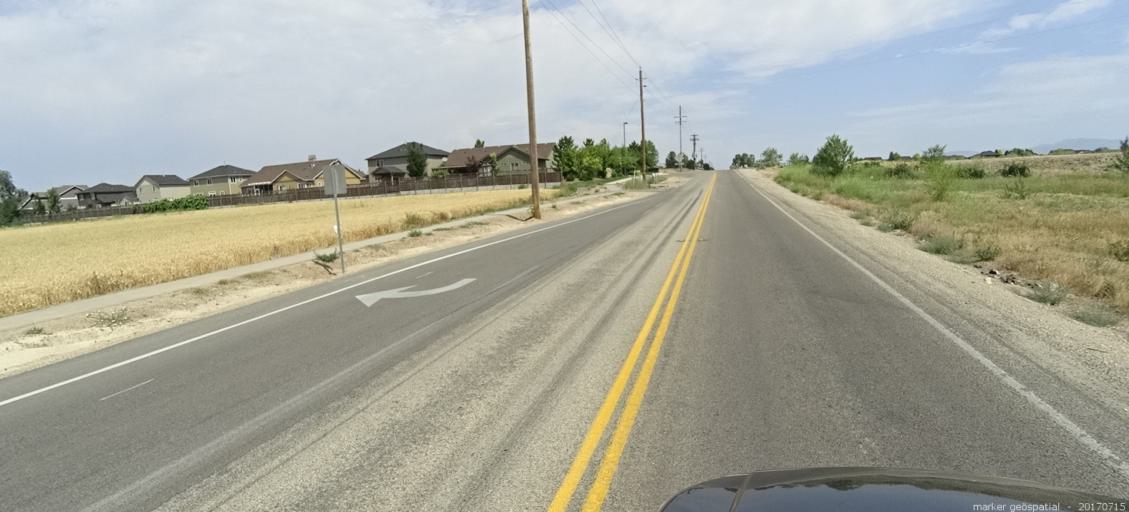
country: US
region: Idaho
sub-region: Ada County
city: Garden City
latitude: 43.5422
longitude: -116.2742
